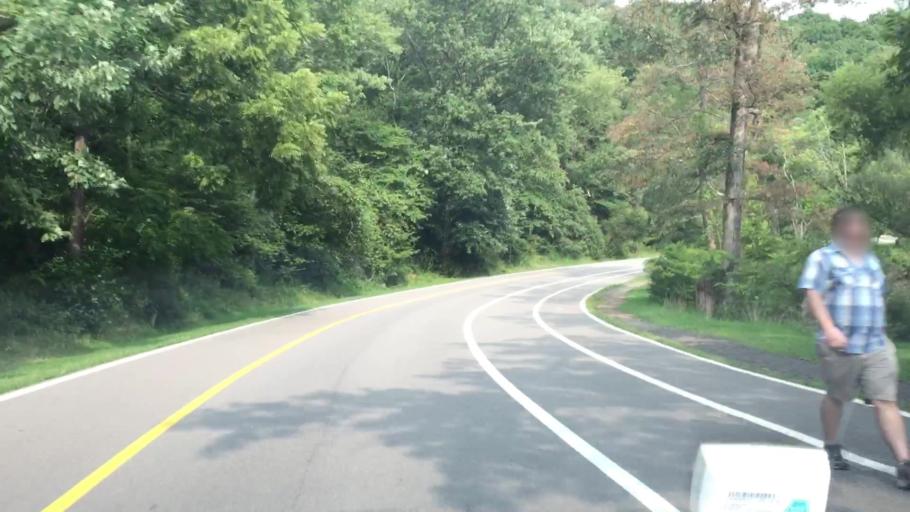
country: US
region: Pennsylvania
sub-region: Allegheny County
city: Gibsonia
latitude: 40.5965
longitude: -80.0071
